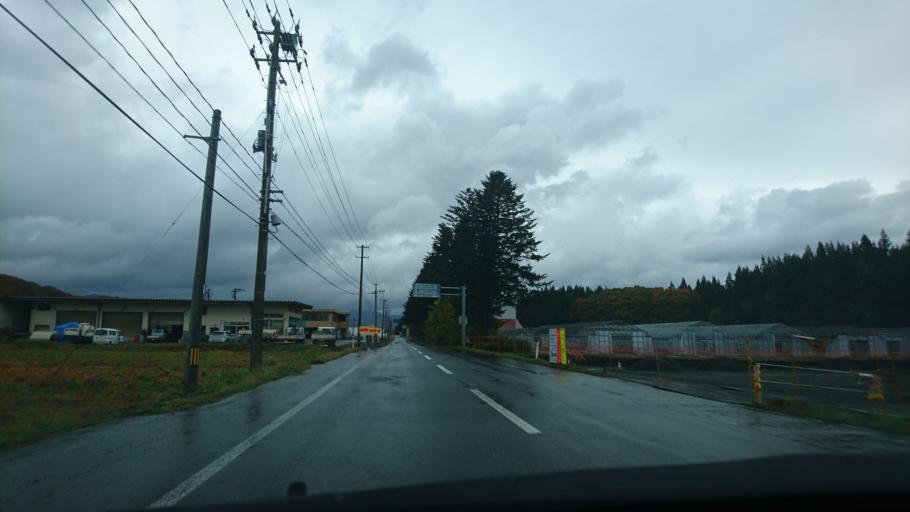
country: JP
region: Akita
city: Yokotemachi
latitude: 39.3727
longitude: 140.7606
